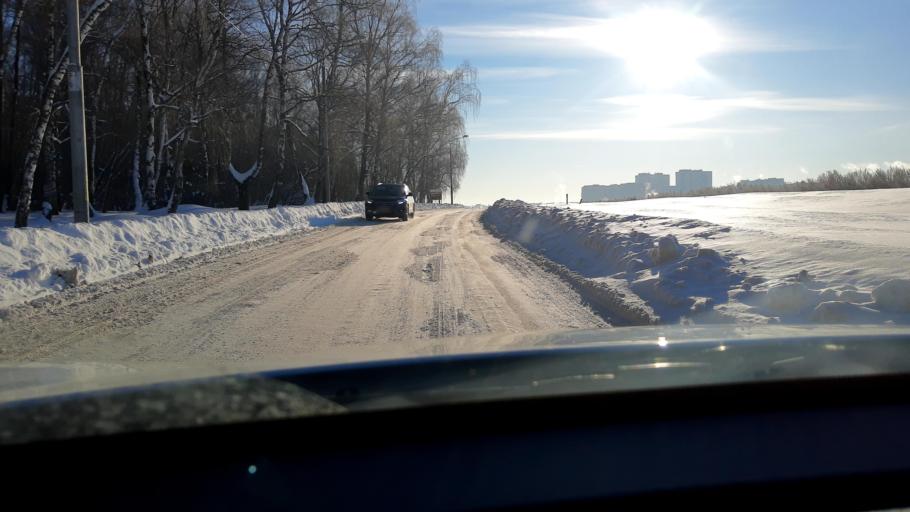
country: RU
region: Moskovskaya
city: Kommunarka
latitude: 55.5411
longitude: 37.4362
